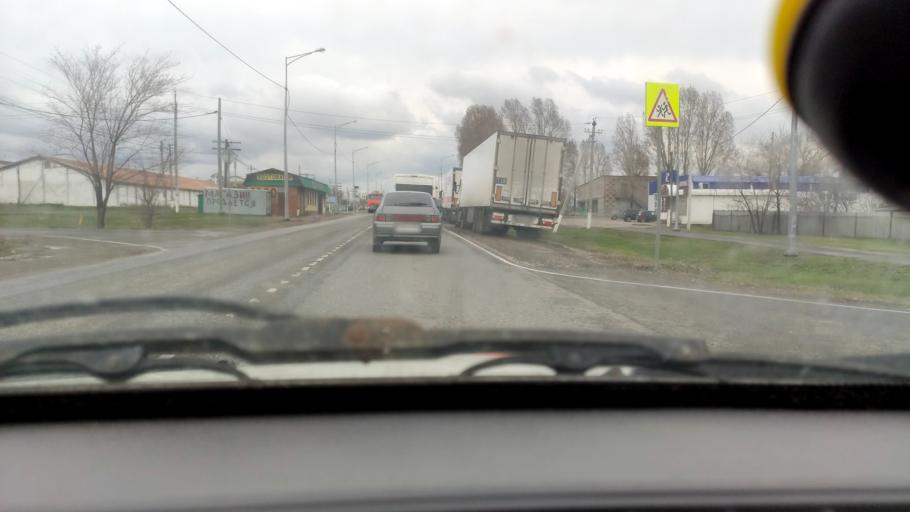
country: RU
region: Samara
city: Zhigulevsk
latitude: 53.5490
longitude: 49.5233
